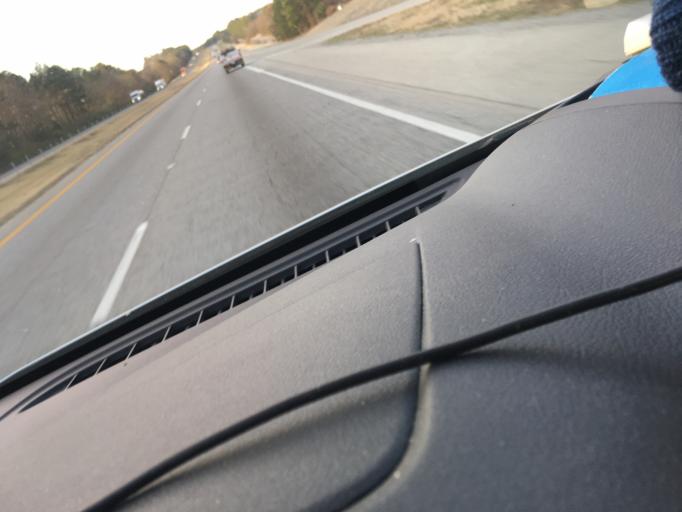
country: US
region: Arkansas
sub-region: Hot Spring County
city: Malvern
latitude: 34.3312
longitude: -92.9216
